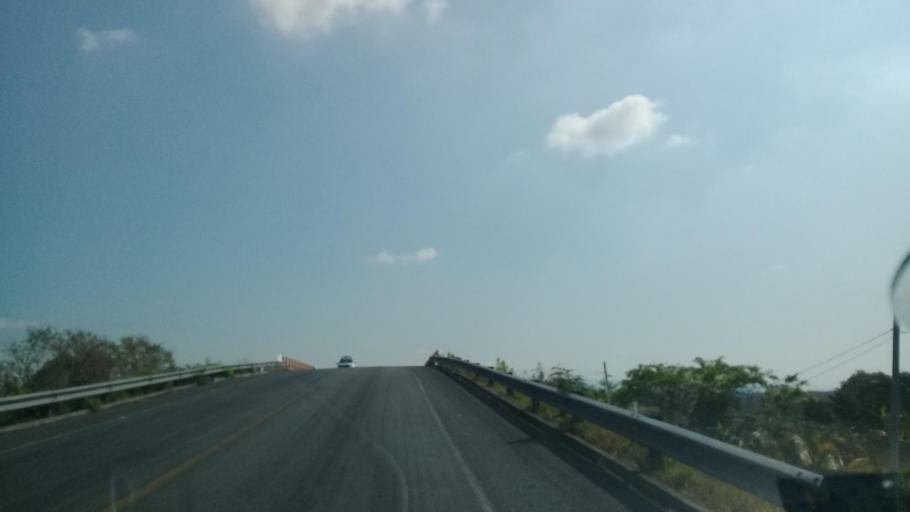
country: MX
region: Veracruz
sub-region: Emiliano Zapata
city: Plan del Rio
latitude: 19.3949
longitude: -96.6184
